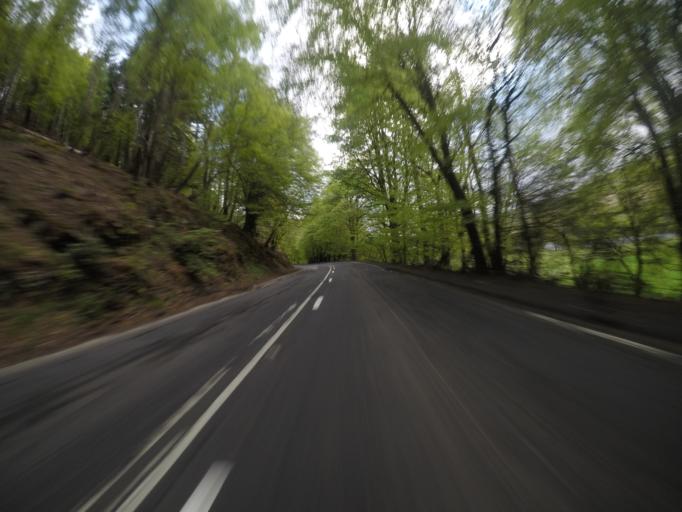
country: GB
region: Scotland
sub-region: Highland
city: Spean Bridge
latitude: 57.0626
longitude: -4.7846
